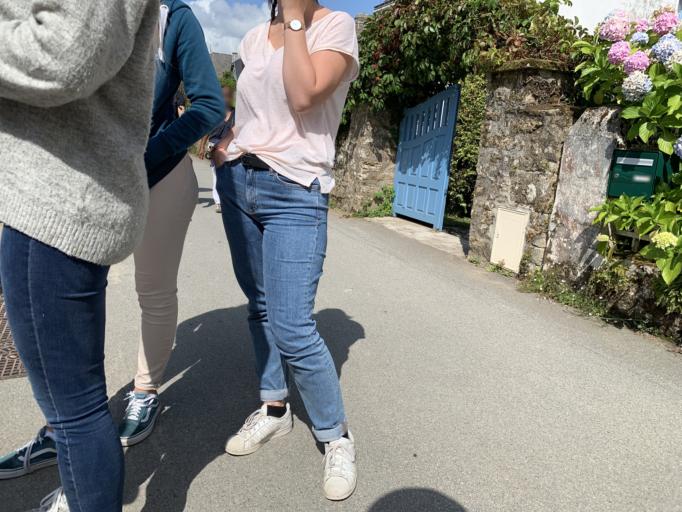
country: FR
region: Brittany
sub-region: Departement du Morbihan
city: Arradon
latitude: 47.5983
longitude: -2.8445
